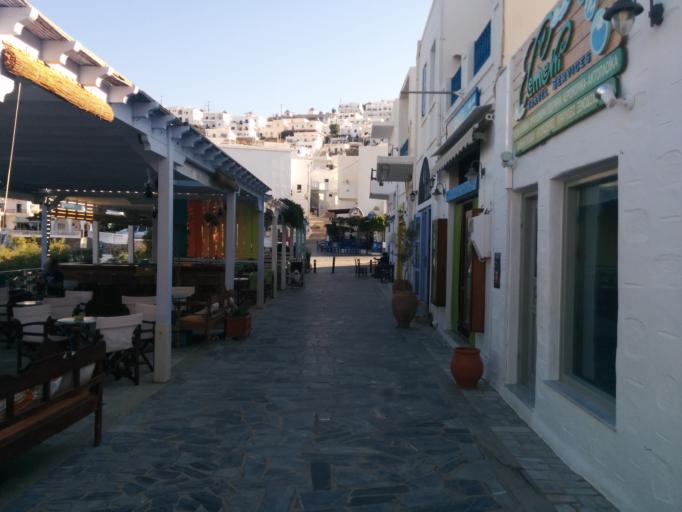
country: GR
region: South Aegean
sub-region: Nomos Dodekanisou
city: Astypalaia
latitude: 36.5489
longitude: 26.3528
